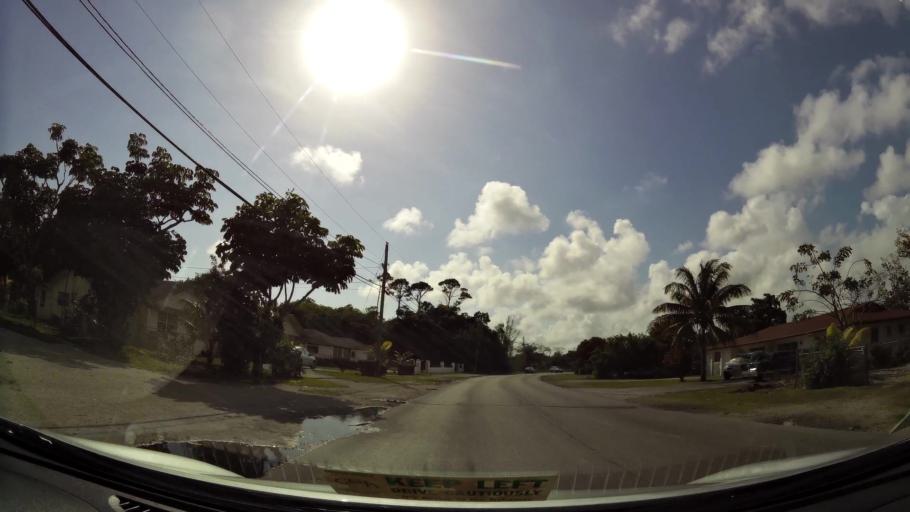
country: BS
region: Freeport
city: Lucaya
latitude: 26.5219
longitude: -78.6802
